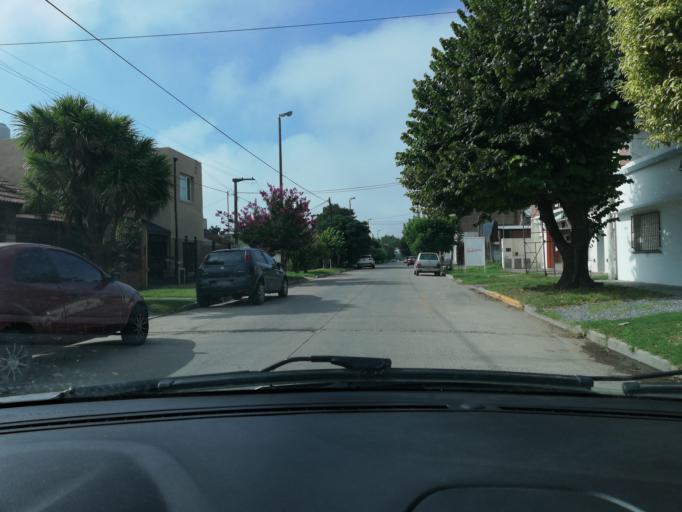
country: AR
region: Buenos Aires
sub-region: Partido de Balcarce
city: Balcarce
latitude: -37.8550
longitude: -58.2467
